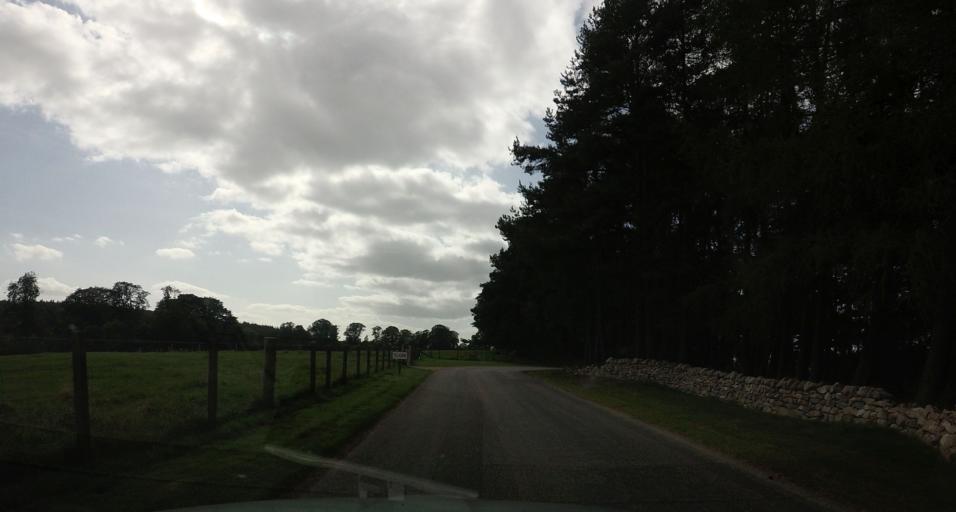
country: GB
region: Scotland
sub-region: Aberdeenshire
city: Kemnay
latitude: 57.2064
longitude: -2.4636
